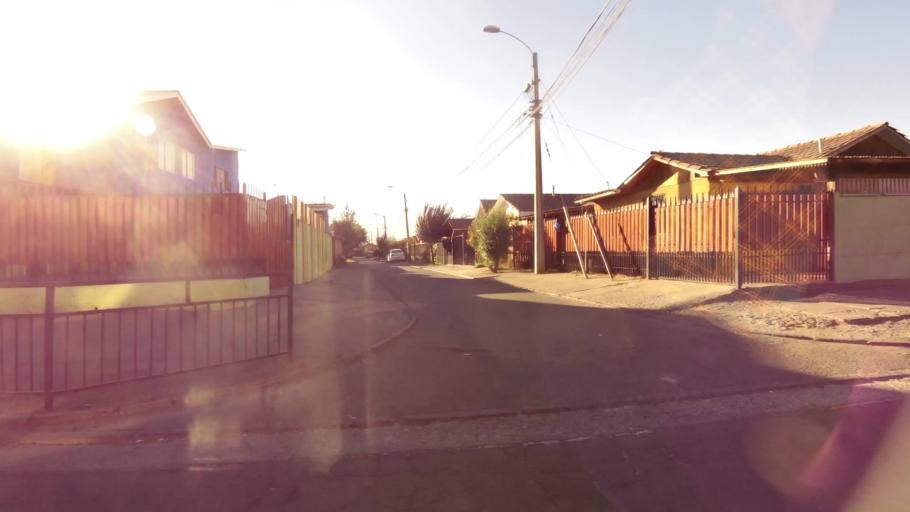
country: CL
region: O'Higgins
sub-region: Provincia de Cachapoal
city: Rancagua
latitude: -34.1818
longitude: -70.7648
